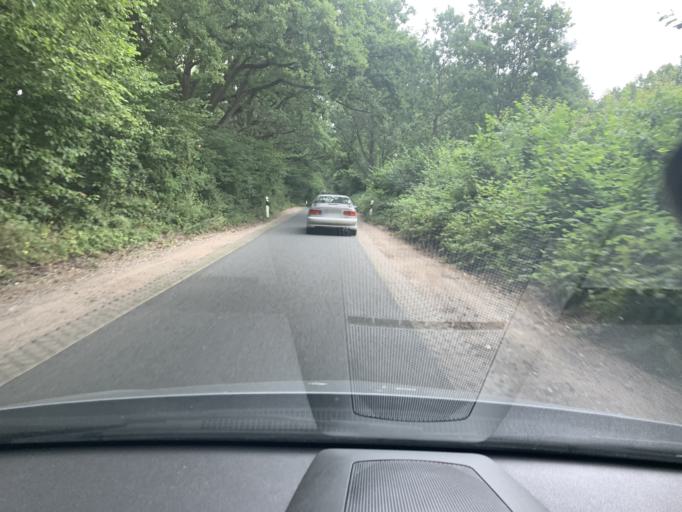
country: DE
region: Schleswig-Holstein
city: Grambek
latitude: 53.5678
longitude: 10.6855
